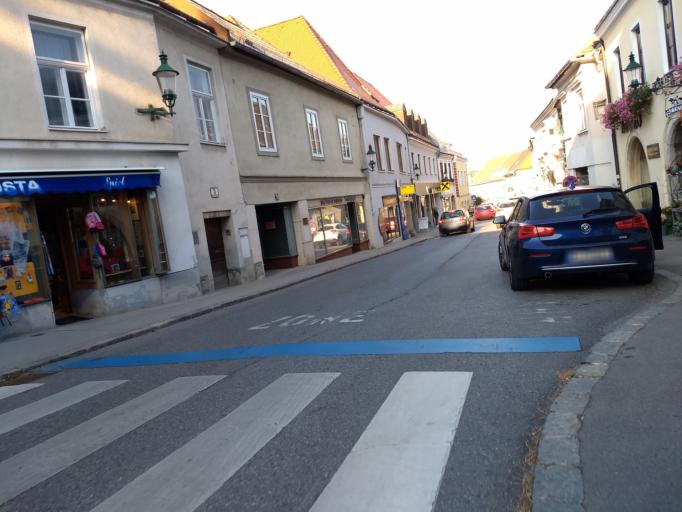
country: AT
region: Lower Austria
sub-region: Politischer Bezirk Modling
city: Perchtoldsdorf
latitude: 48.1202
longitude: 16.2652
